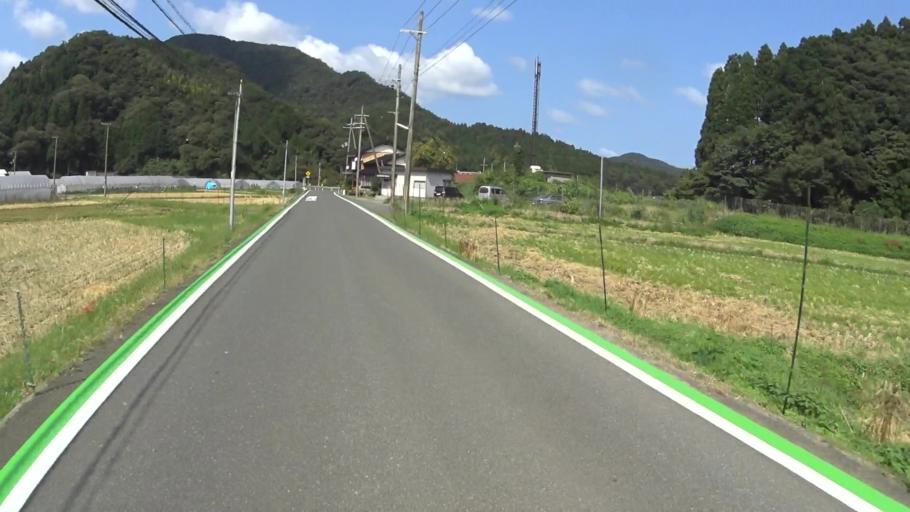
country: JP
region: Kyoto
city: Miyazu
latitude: 35.7164
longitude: 135.2526
